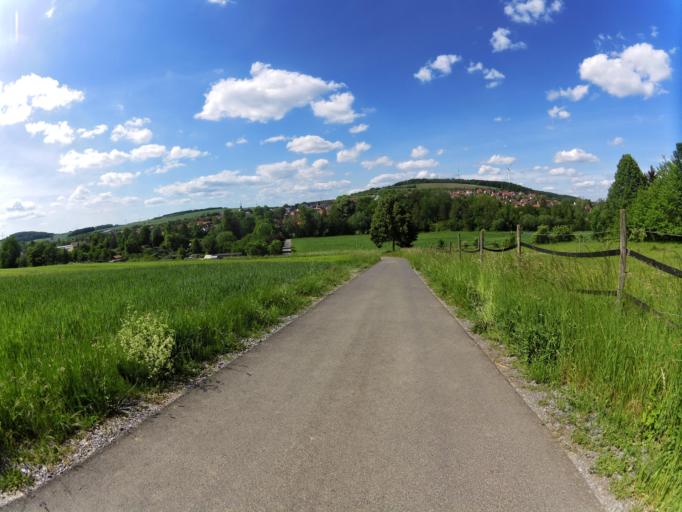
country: DE
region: Bavaria
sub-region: Regierungsbezirk Unterfranken
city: Uettingen
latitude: 49.7915
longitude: 9.7333
